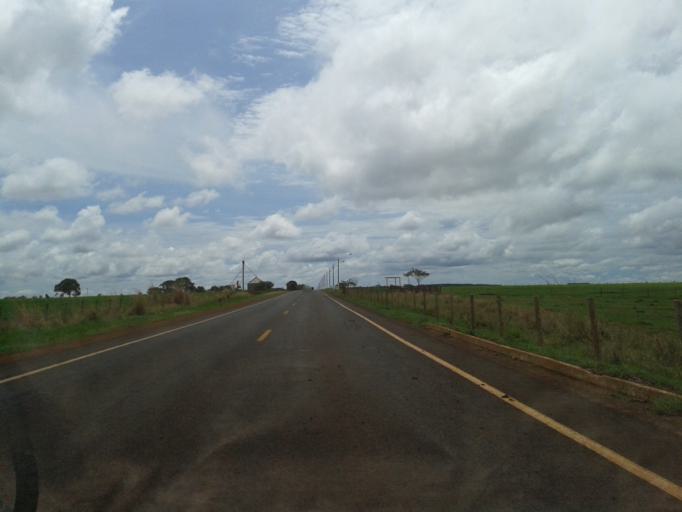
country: BR
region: Goias
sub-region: Buriti Alegre
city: Buriti Alegre
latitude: -18.1356
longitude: -49.0200
